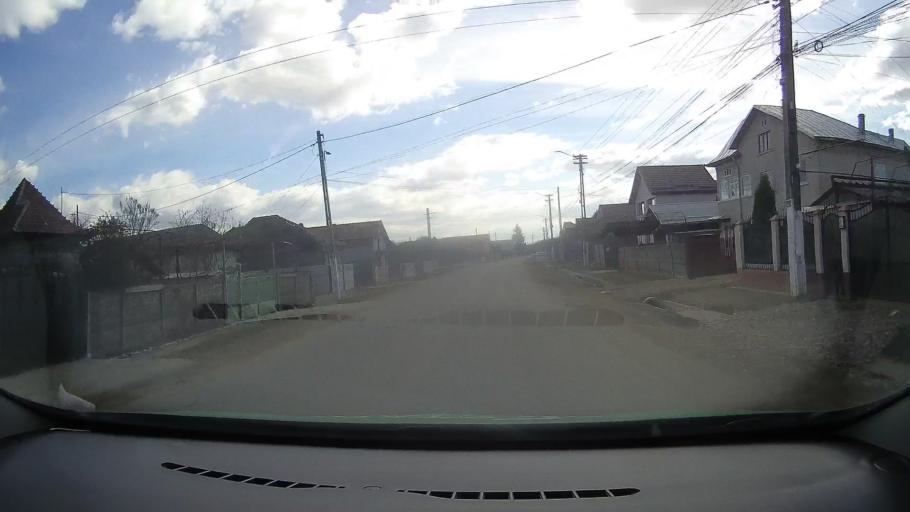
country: RO
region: Dambovita
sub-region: Comuna Doicesti
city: Doicesti
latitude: 44.9802
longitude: 25.3902
